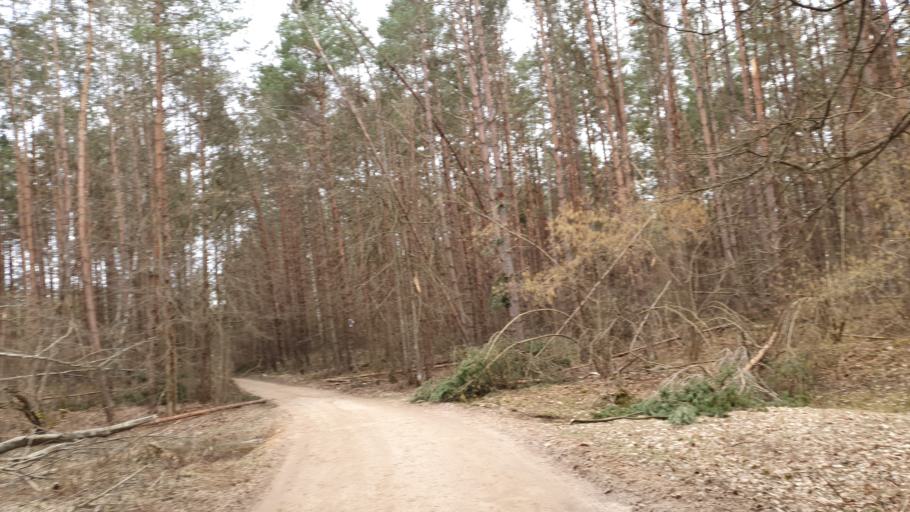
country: LT
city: Grigiskes
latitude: 54.7317
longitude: 25.0280
